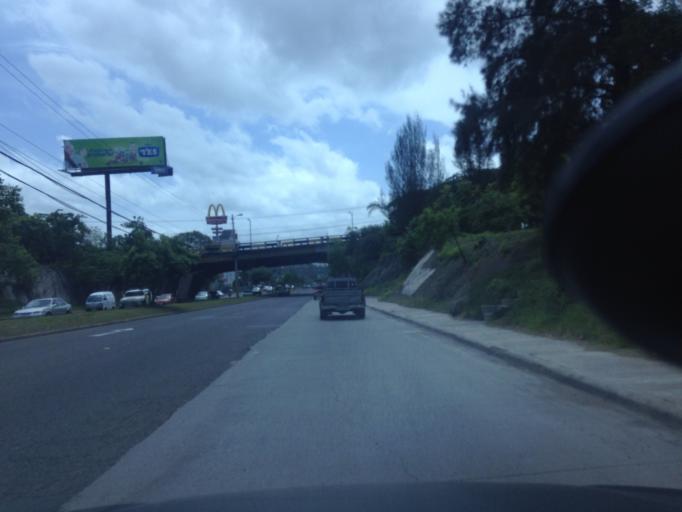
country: HN
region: Francisco Morazan
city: Tegucigalpa
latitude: 14.0734
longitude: -87.2027
